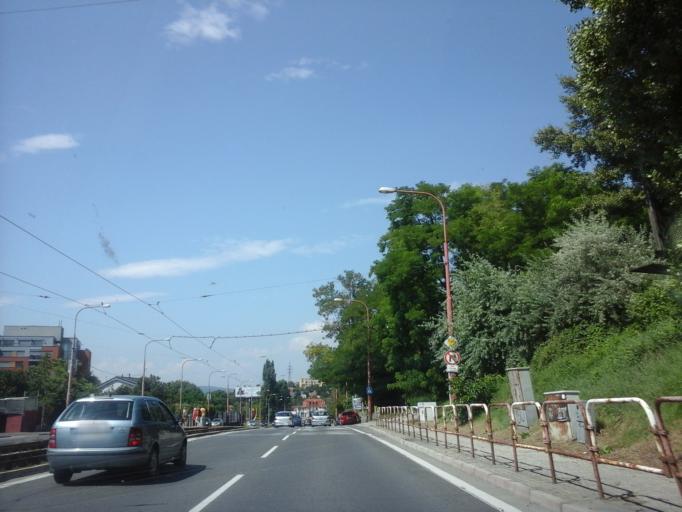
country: SK
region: Bratislavsky
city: Bratislava
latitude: 48.1483
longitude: 17.0689
